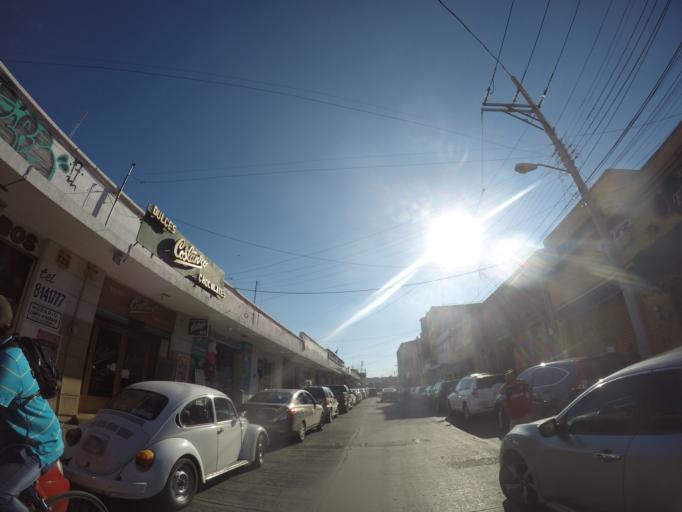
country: MX
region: San Luis Potosi
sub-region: San Luis Potosi
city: San Luis Potosi
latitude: 22.1555
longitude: -100.9779
